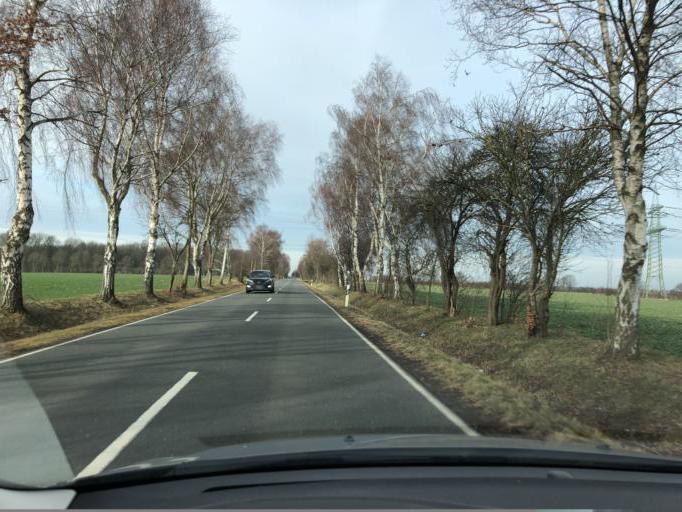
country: DE
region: Saxony-Anhalt
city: Eckartsberga
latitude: 51.1825
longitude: 11.5059
